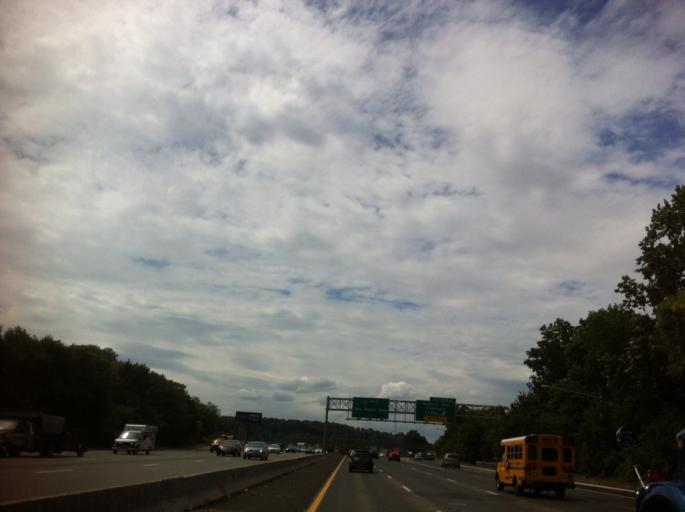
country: US
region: New Jersey
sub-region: Bergen County
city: Elmwood Park
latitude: 40.9018
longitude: -74.1313
